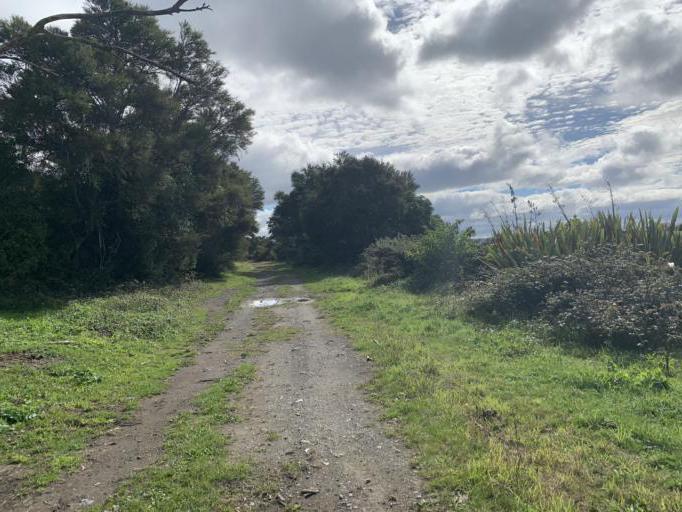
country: NZ
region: Waikato
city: Turangi
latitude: -38.9740
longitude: 175.7774
